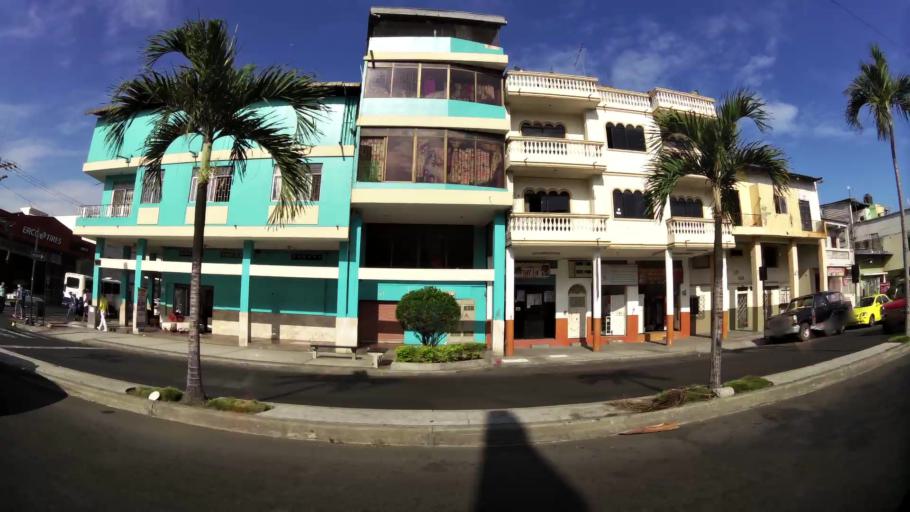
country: EC
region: Guayas
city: Guayaquil
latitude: -2.1971
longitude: -79.9146
